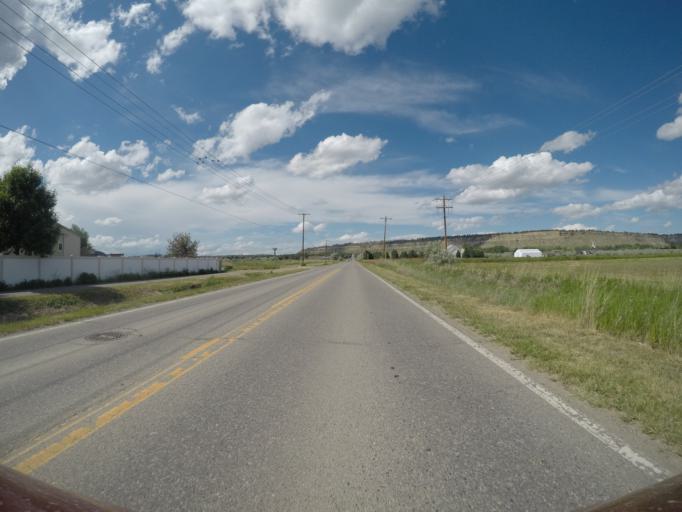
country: US
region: Montana
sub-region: Yellowstone County
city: Billings
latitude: 45.7909
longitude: -108.6527
